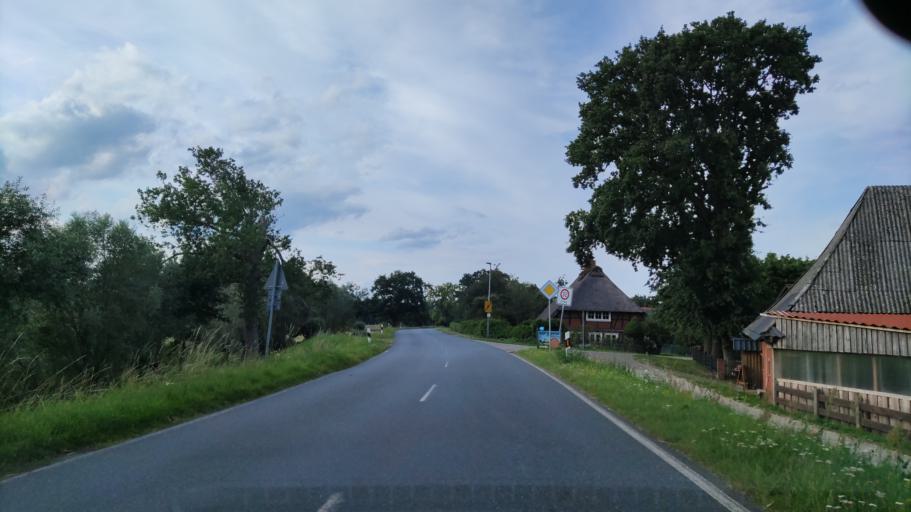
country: DE
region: Lower Saxony
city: Dannenberg
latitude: 53.1355
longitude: 11.1221
